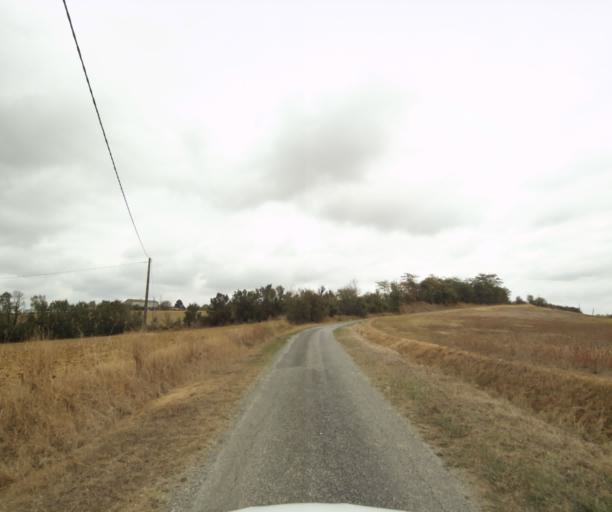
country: FR
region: Midi-Pyrenees
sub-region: Departement de la Haute-Garonne
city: Villefranche-de-Lauragais
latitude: 43.4178
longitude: 1.7330
